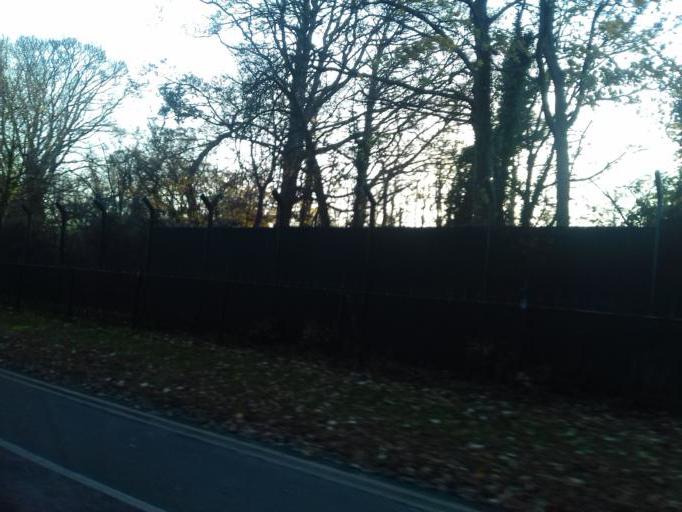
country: IE
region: Leinster
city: Cabra
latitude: 53.3580
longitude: -6.3045
